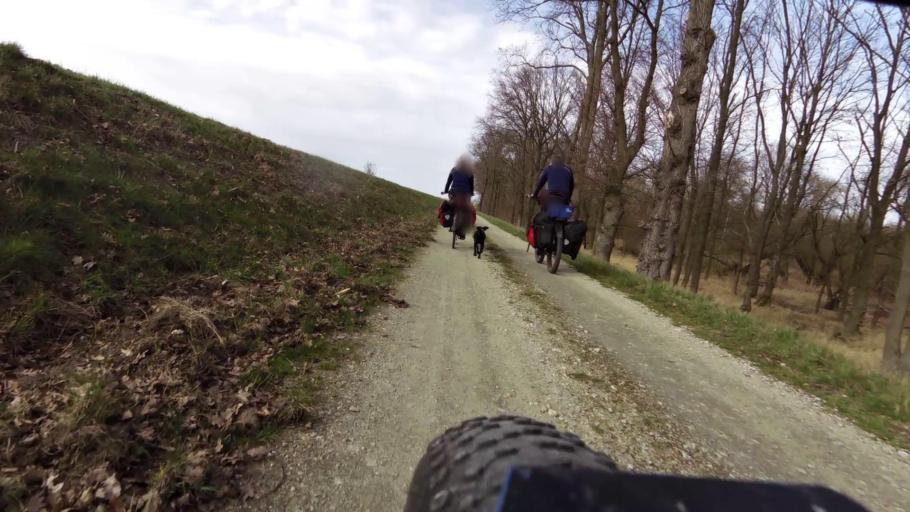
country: DE
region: Brandenburg
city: Reitwein
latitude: 52.5209
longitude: 14.6114
